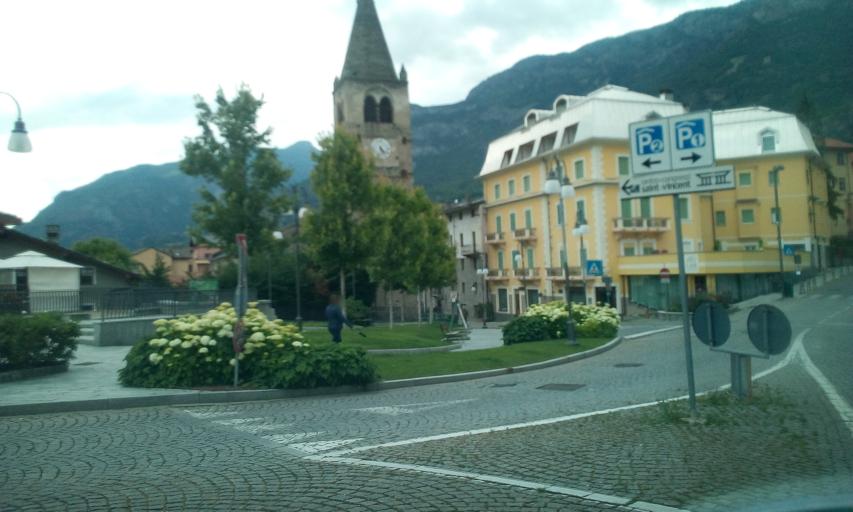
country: IT
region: Aosta Valley
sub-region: Valle d'Aosta
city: Saint-Vincent
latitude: 45.7504
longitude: 7.6506
